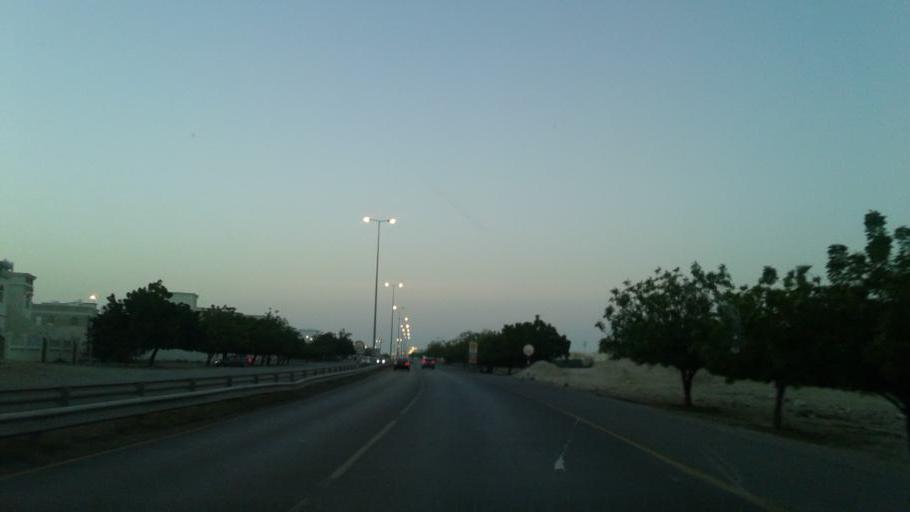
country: OM
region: Muhafazat Masqat
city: As Sib al Jadidah
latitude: 23.6057
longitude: 58.2173
